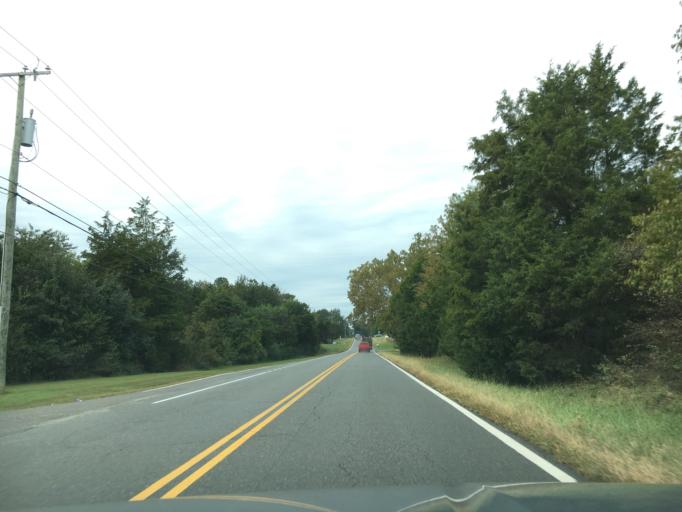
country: US
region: Virginia
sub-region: Goochland County
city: Goochland
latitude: 37.7508
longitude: -77.8599
